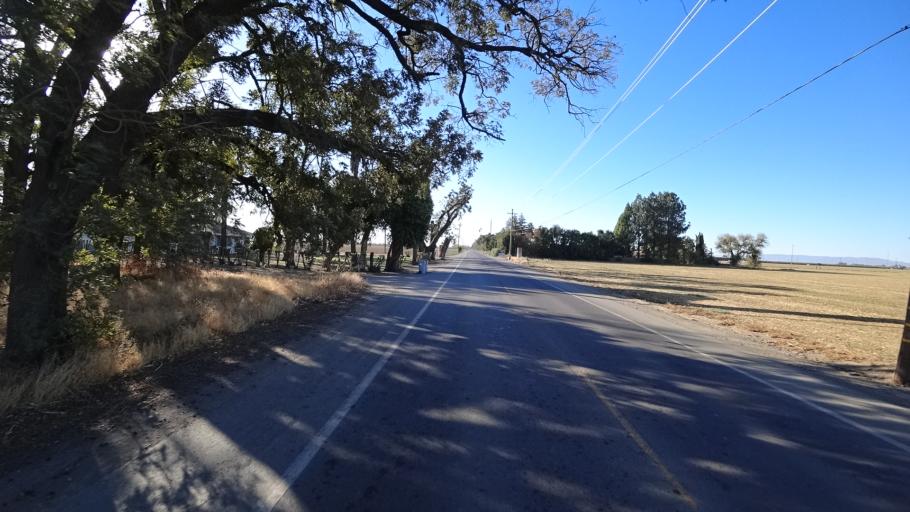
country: US
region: California
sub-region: Yolo County
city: Woodland
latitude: 38.6501
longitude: -121.7844
